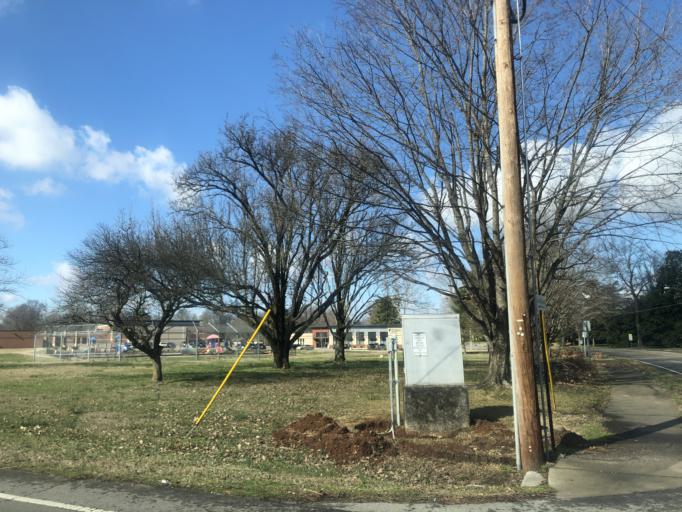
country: US
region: Tennessee
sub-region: Rutherford County
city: Murfreesboro
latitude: 35.8380
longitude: -86.3633
